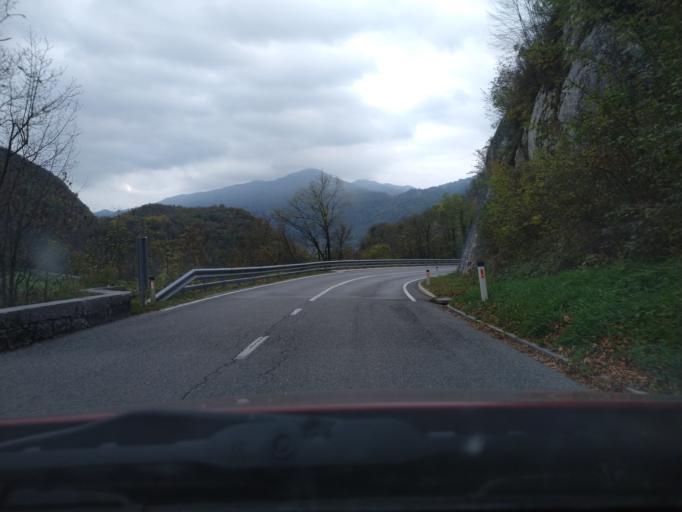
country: SI
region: Kobarid
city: Kobarid
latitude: 46.2545
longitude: 13.5831
